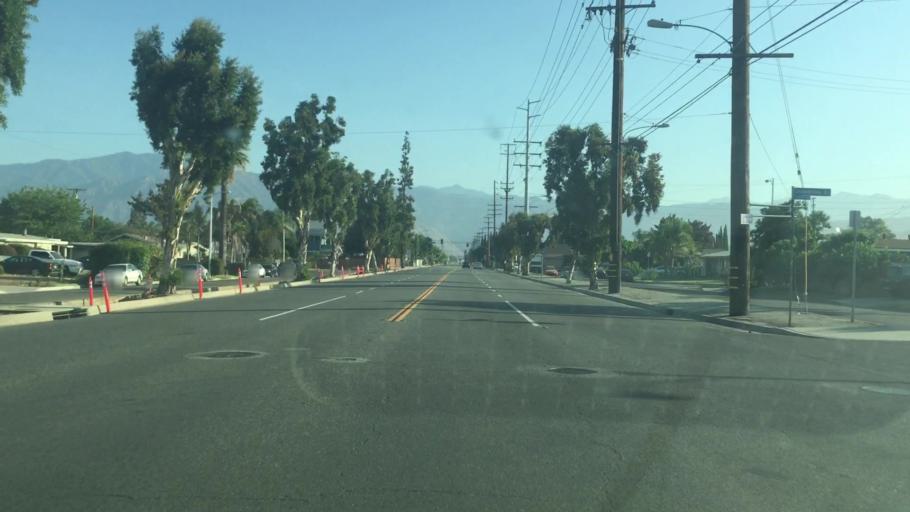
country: US
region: California
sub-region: Los Angeles County
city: Irwindale
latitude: 34.0937
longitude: -117.9254
